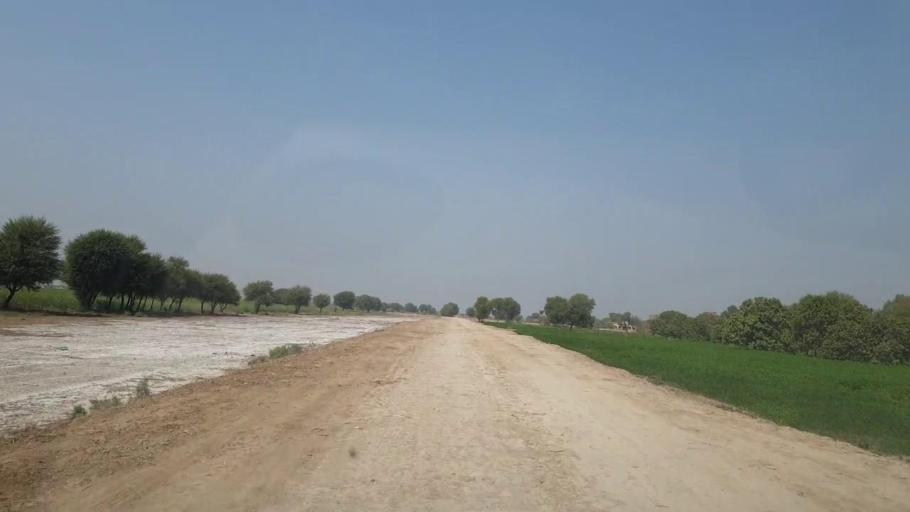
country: PK
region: Sindh
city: Mirpur Khas
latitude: 25.6555
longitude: 69.1354
